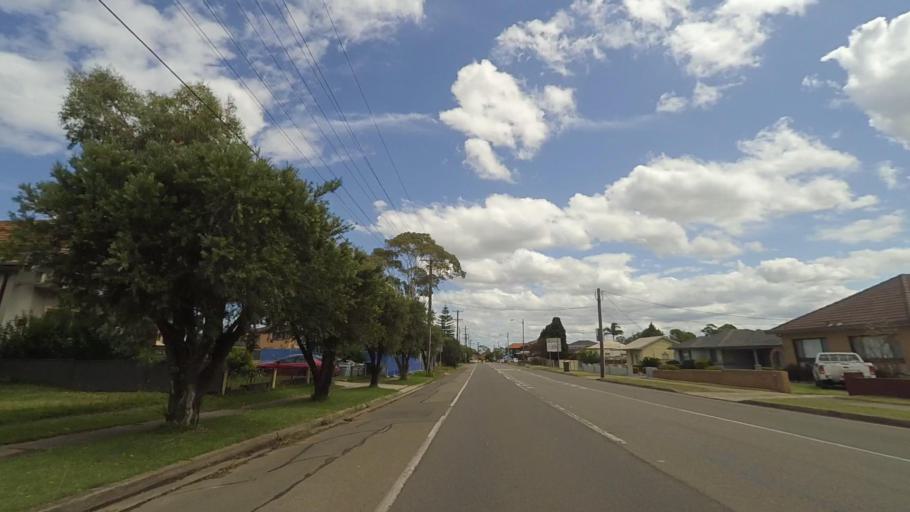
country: AU
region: New South Wales
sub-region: Holroyd
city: Guildford West
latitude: -33.8487
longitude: 150.9617
